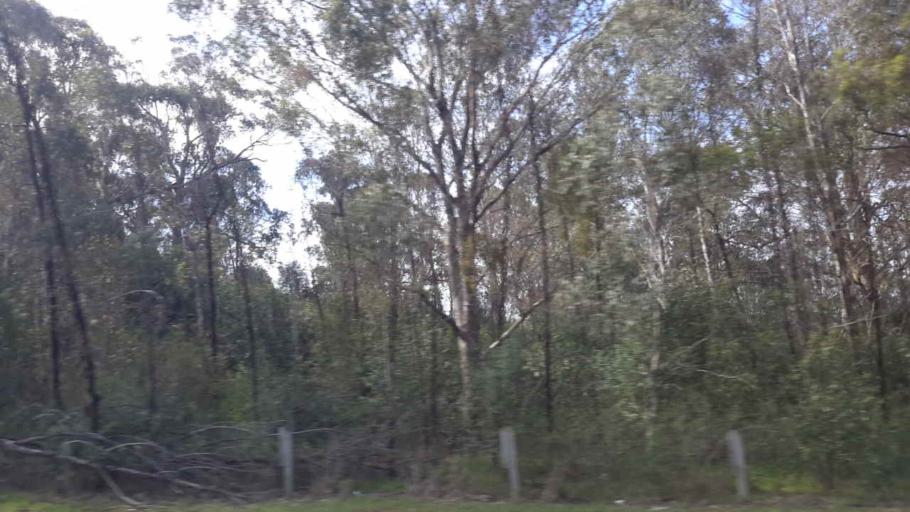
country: AU
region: New South Wales
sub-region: Campbelltown Municipality
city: Glen Alpine
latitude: -34.0798
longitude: 150.8000
